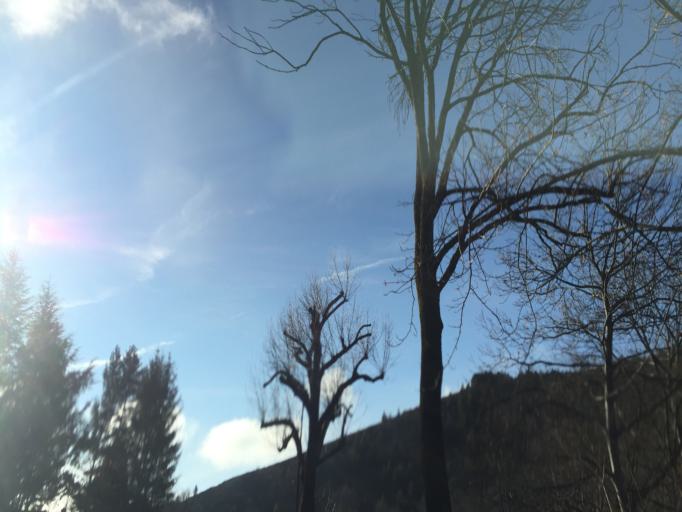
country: FR
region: Languedoc-Roussillon
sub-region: Departement de la Lozere
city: Langogne
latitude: 44.5178
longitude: 3.9090
